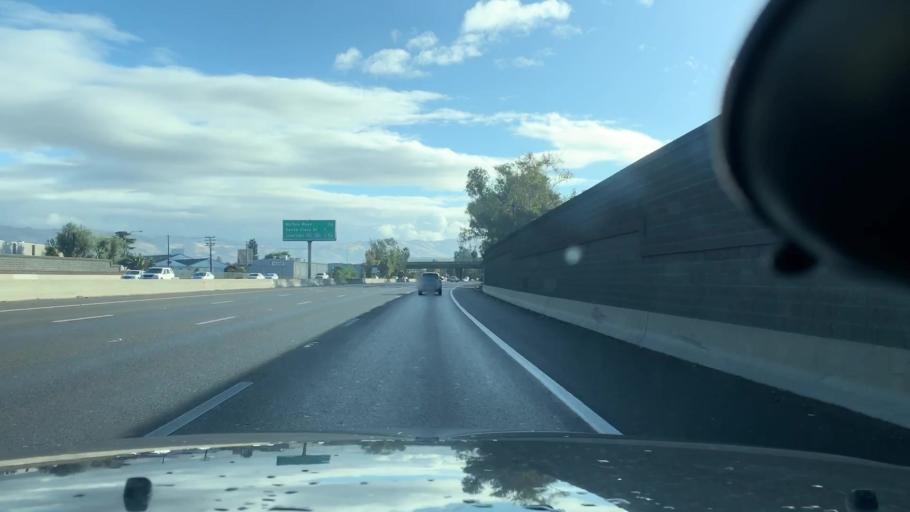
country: US
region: California
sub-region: Santa Clara County
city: San Jose
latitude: 37.3615
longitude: -121.8817
